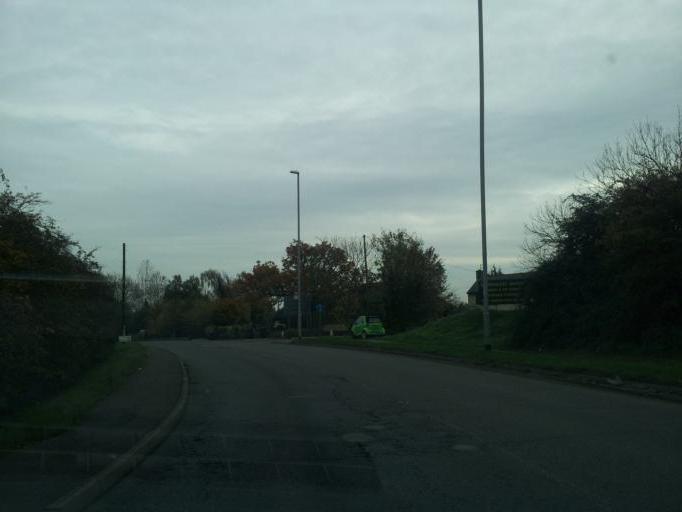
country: GB
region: England
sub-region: Cambridgeshire
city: Comberton
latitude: 52.2158
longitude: 0.0393
